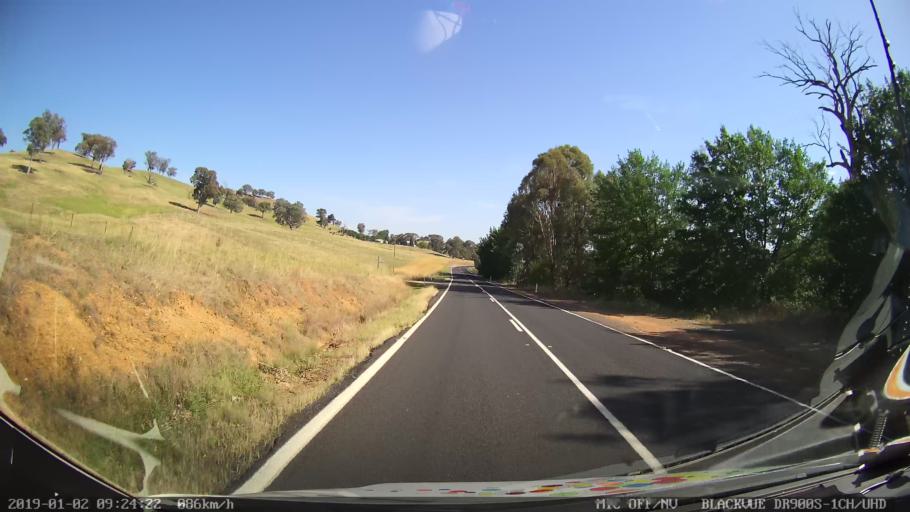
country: AU
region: New South Wales
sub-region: Tumut Shire
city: Tumut
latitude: -35.3780
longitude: 148.2920
